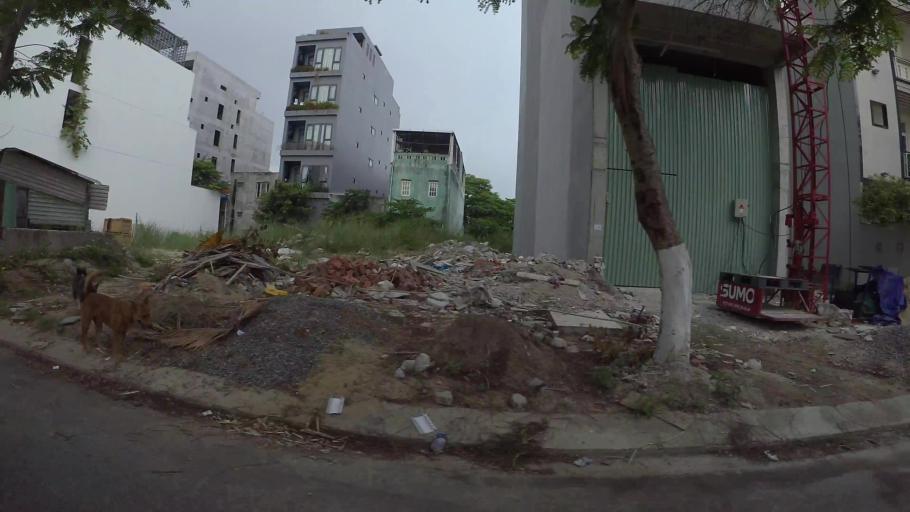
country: VN
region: Da Nang
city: Son Tra
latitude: 16.0795
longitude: 108.2445
